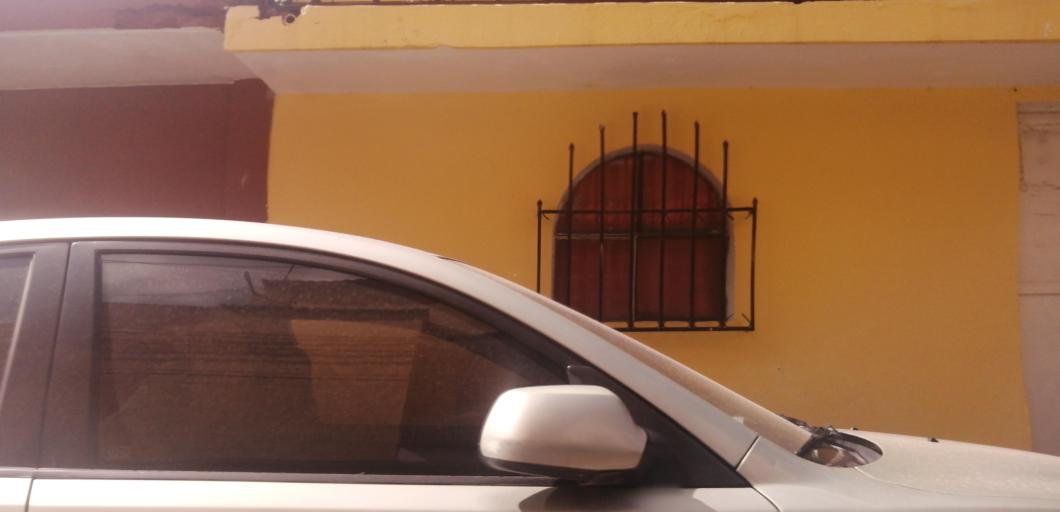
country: GT
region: Quetzaltenango
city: Quetzaltenango
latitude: 14.8428
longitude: -91.5330
